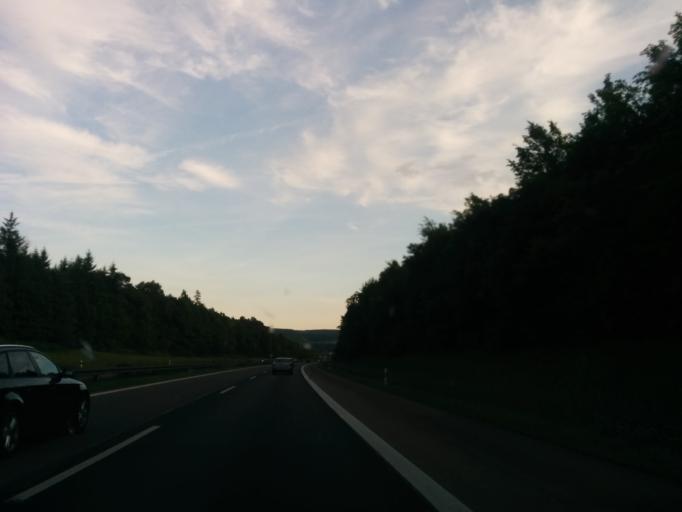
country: DE
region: Bavaria
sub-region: Regierungsbezirk Unterfranken
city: Elfershausen
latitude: 50.1683
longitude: 9.9635
